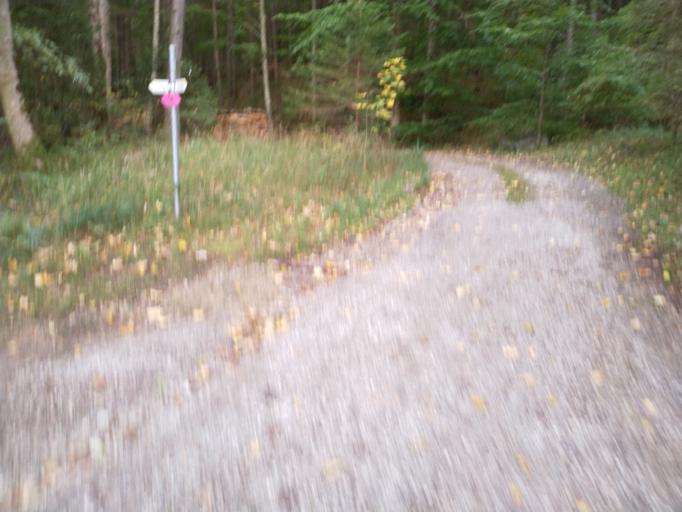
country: AT
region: Tyrol
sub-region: Politischer Bezirk Reutte
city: Vils
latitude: 47.5675
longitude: 10.6416
